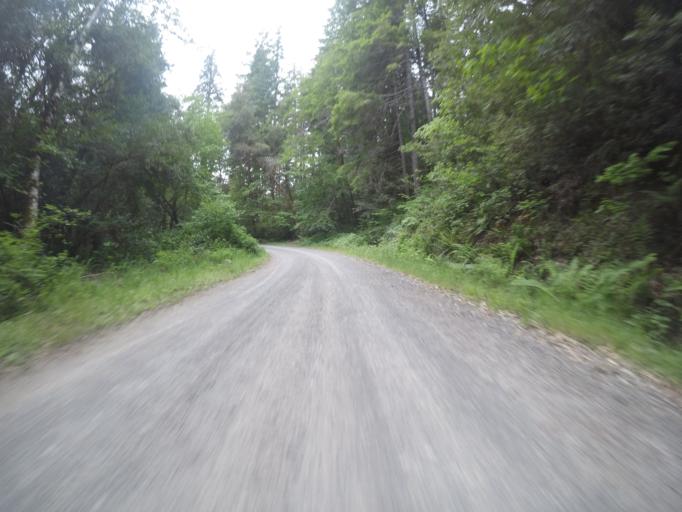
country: US
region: California
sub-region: Del Norte County
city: Bertsch-Oceanview
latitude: 41.7196
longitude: -123.8982
